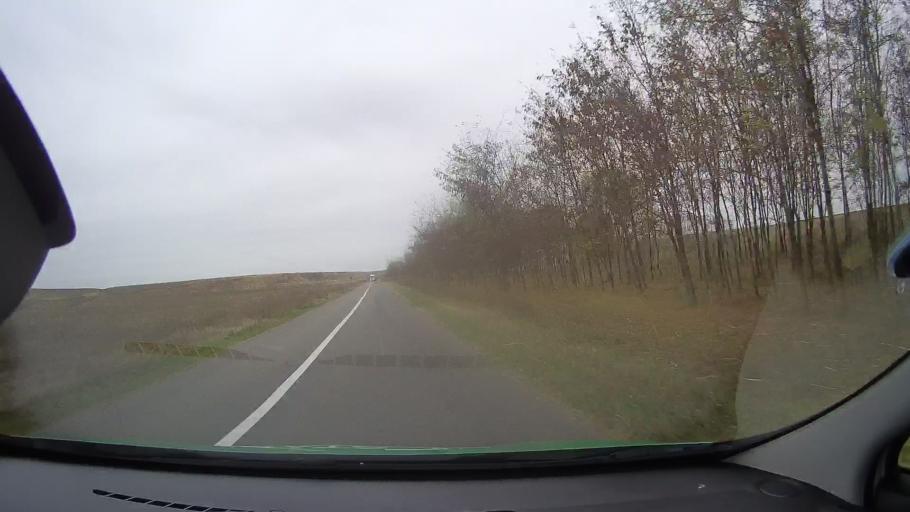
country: RO
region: Constanta
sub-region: Comuna Saraiu
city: Saraiu
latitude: 44.7264
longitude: 28.1786
